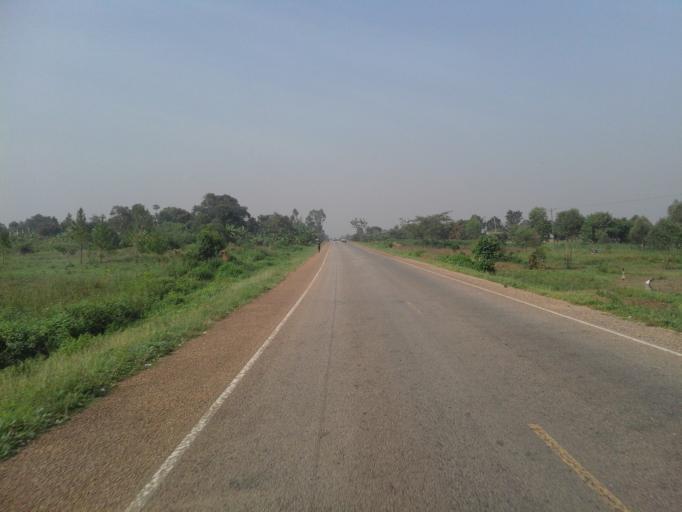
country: UG
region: Eastern Region
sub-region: Budaka District
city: Budaka
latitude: 1.0327
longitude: 33.9914
